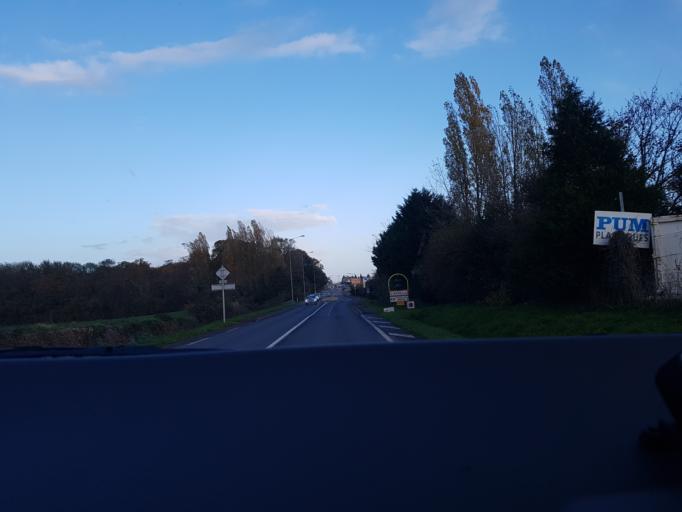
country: FR
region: Lower Normandy
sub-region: Departement du Calvados
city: Giberville
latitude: 49.1722
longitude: -0.2876
